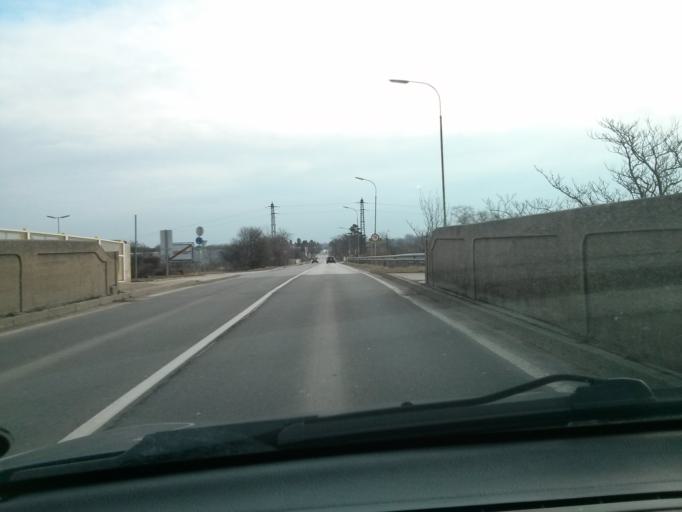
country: AT
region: Lower Austria
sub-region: Politischer Bezirk Baden
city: Kottingbrunn
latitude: 47.9372
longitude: 16.2317
